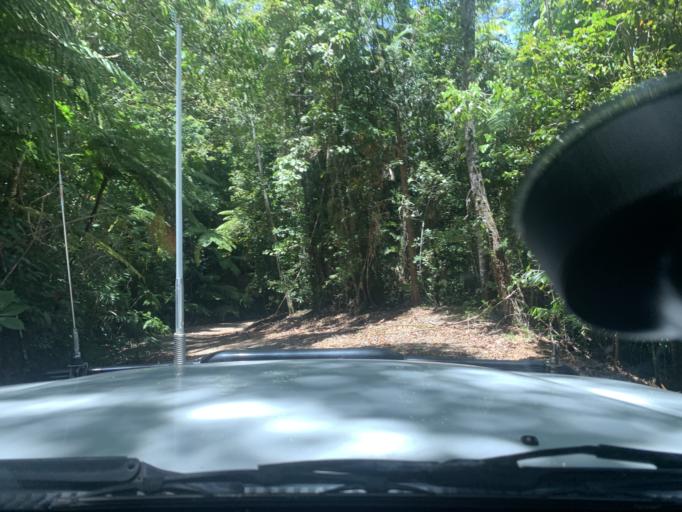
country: AU
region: Queensland
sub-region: Cairns
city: Redlynch
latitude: -16.9720
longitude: 145.6500
